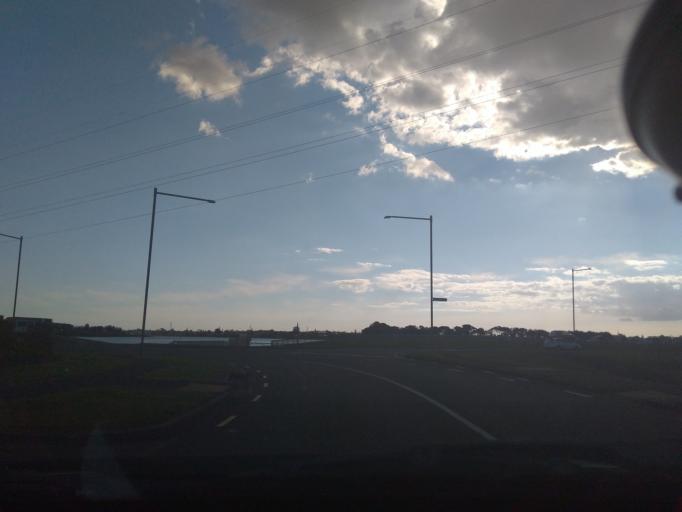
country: NZ
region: Auckland
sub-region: Auckland
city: Tamaki
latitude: -36.9312
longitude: 174.8714
